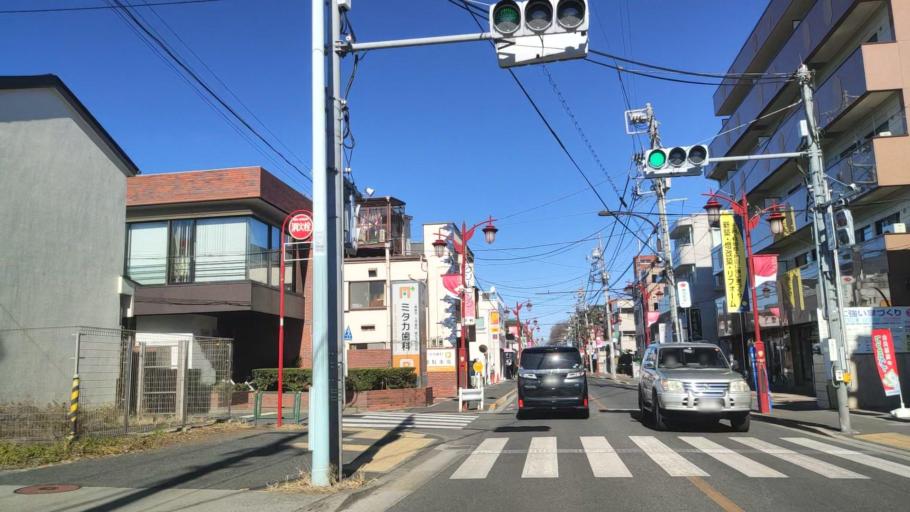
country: JP
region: Tokyo
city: Mitaka-shi
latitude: 35.6923
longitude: 139.5695
